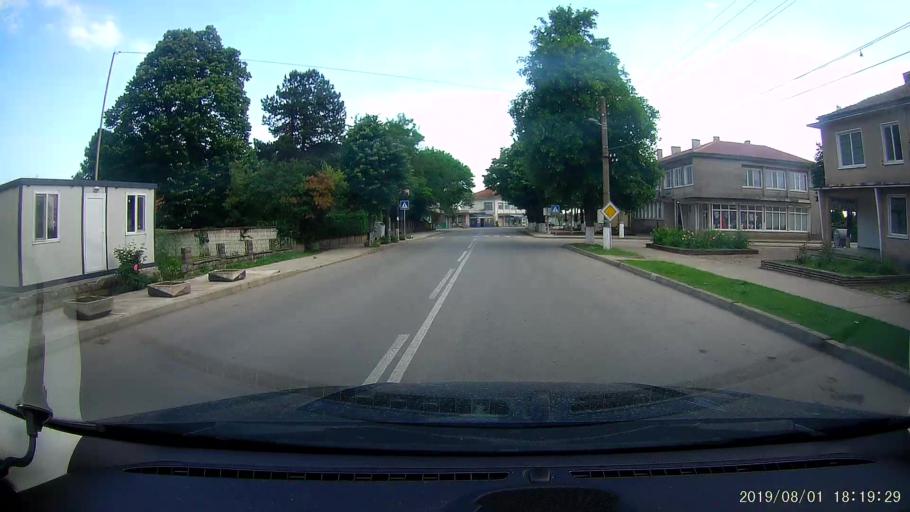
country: BG
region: Shumen
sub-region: Obshtina Kaolinovo
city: Kaolinovo
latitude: 43.6830
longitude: 27.0909
